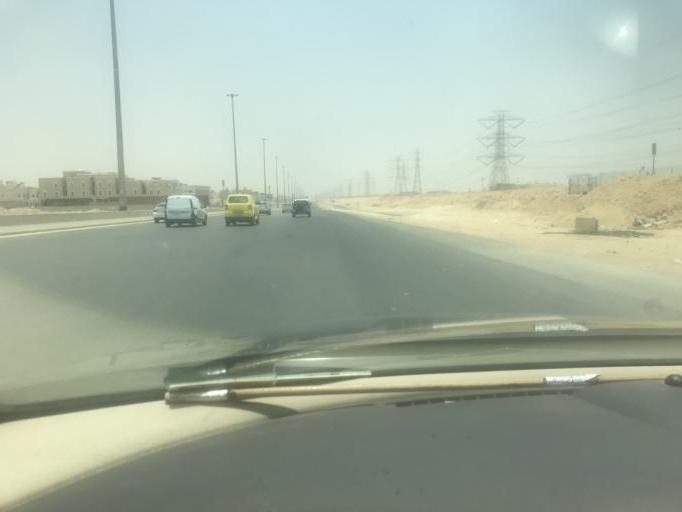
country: SA
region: Ar Riyad
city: Riyadh
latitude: 24.8169
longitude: 46.7332
